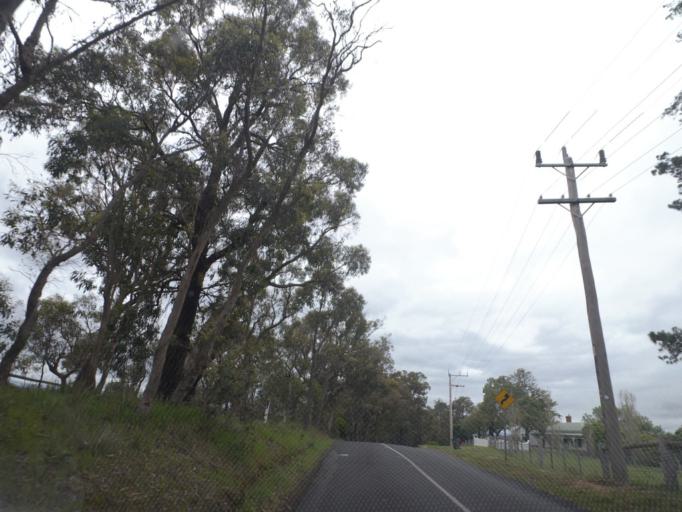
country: AU
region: Victoria
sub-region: Nillumbik
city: Hurstbridge
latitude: -37.6548
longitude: 145.2377
